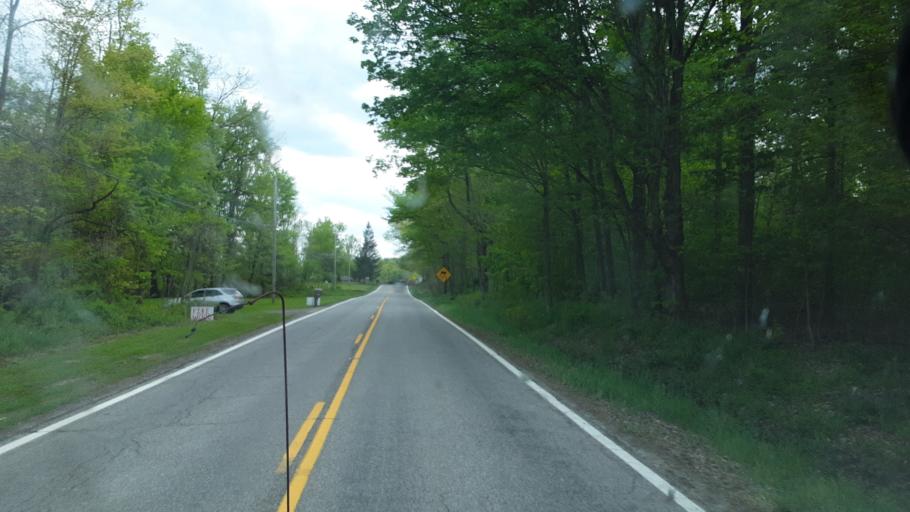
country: US
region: Ohio
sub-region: Portage County
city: Garrettsville
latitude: 41.3502
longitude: -81.0387
